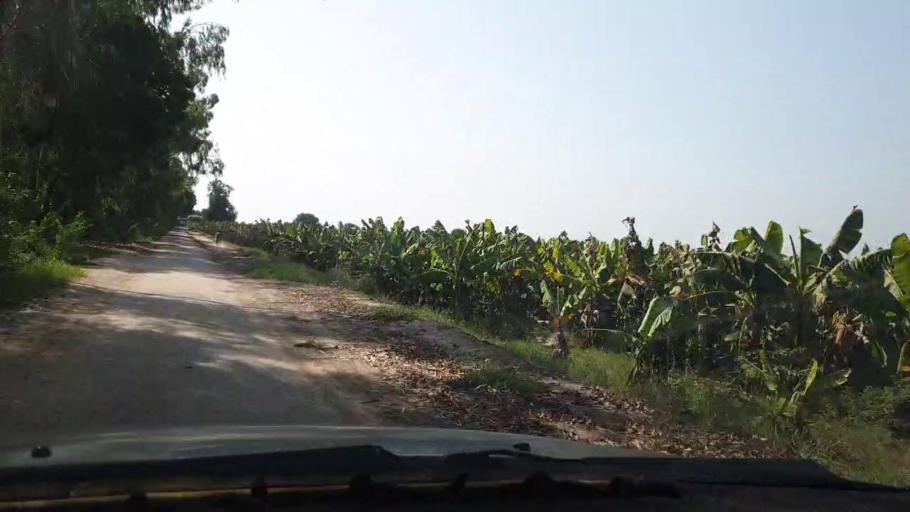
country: PK
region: Sindh
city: Chambar
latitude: 25.2446
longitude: 68.9101
